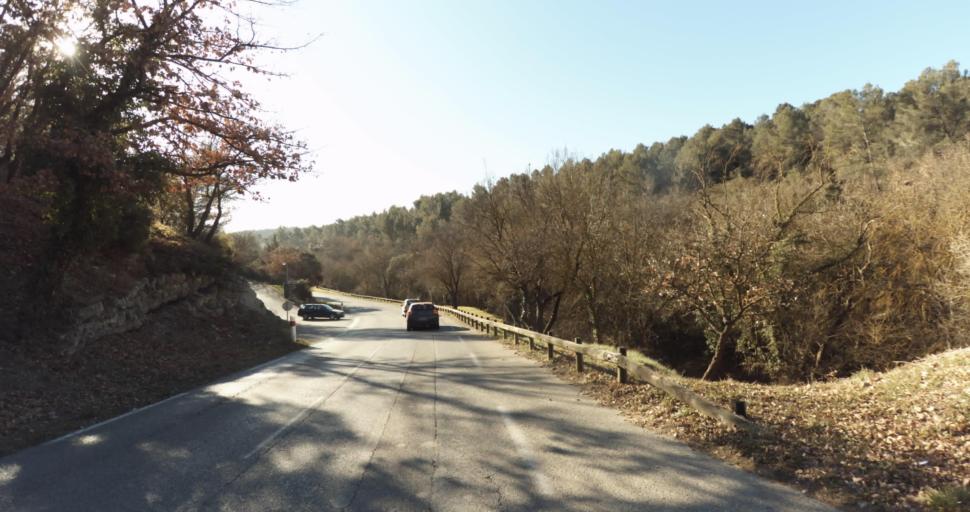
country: FR
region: Provence-Alpes-Cote d'Azur
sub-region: Departement des Bouches-du-Rhone
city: Cadolive
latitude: 43.4047
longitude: 5.5573
